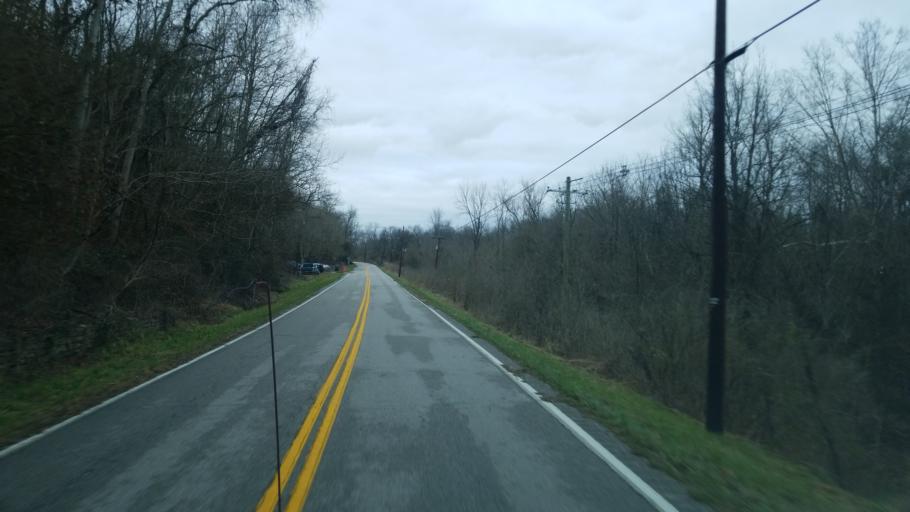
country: US
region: Ohio
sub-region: Clermont County
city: New Richmond
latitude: 38.9173
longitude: -84.2667
